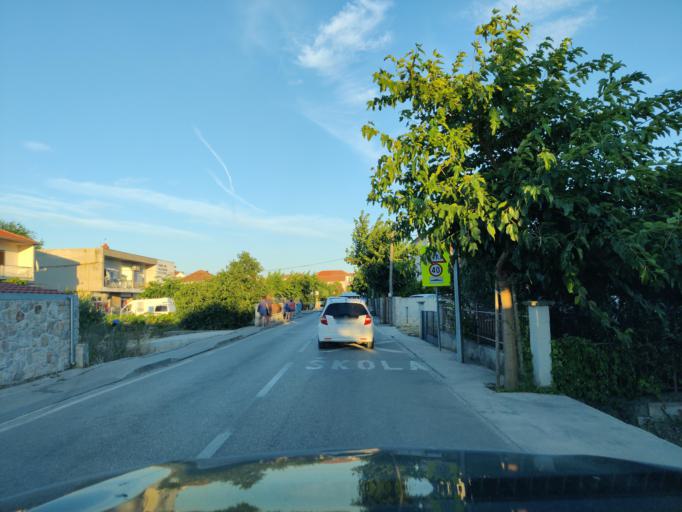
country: HR
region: Sibensko-Kniniska
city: Murter
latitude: 43.8247
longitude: 15.6010
